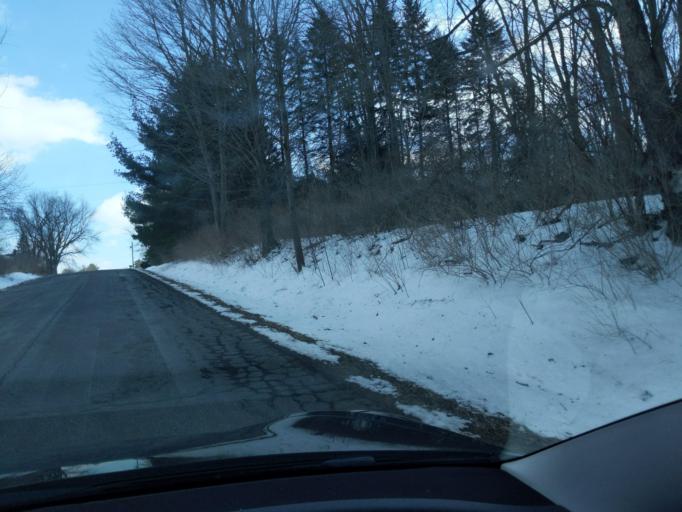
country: US
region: Michigan
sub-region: Ingham County
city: Mason
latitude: 42.6109
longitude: -84.3922
